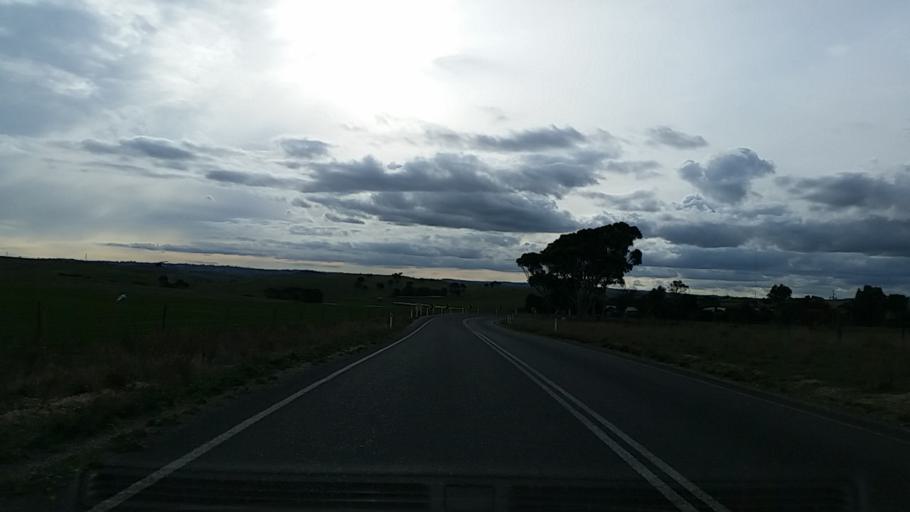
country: AU
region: South Australia
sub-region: Mount Barker
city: Callington
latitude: -35.0634
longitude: 139.0420
